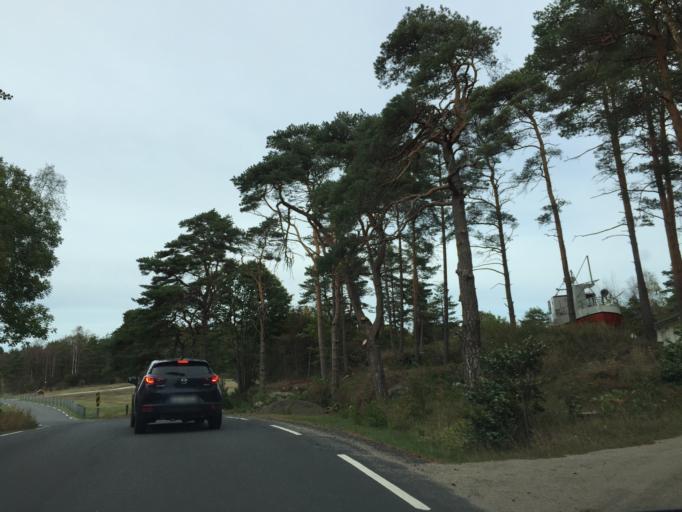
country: NO
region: Ostfold
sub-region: Hvaler
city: Skjaerhalden
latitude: 59.0371
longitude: 11.0277
